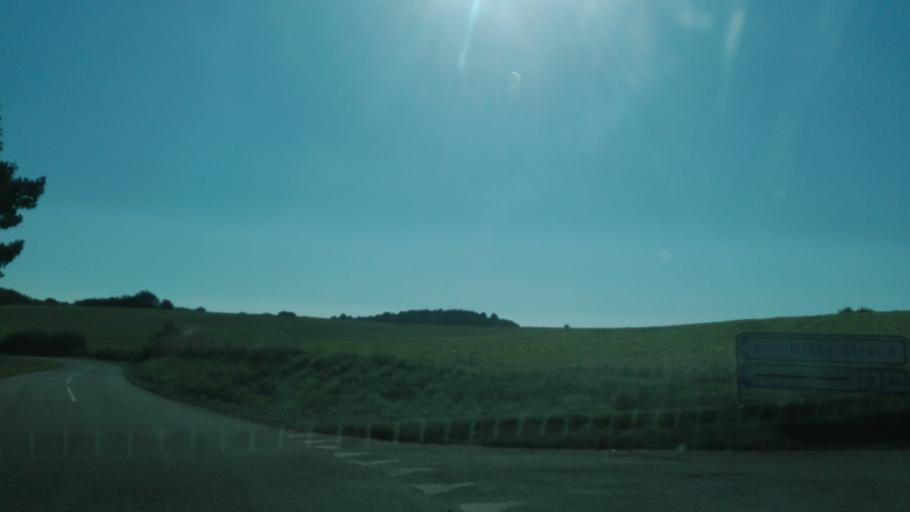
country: DK
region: Central Jutland
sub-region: Syddjurs Kommune
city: Ebeltoft
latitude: 56.2216
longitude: 10.7048
